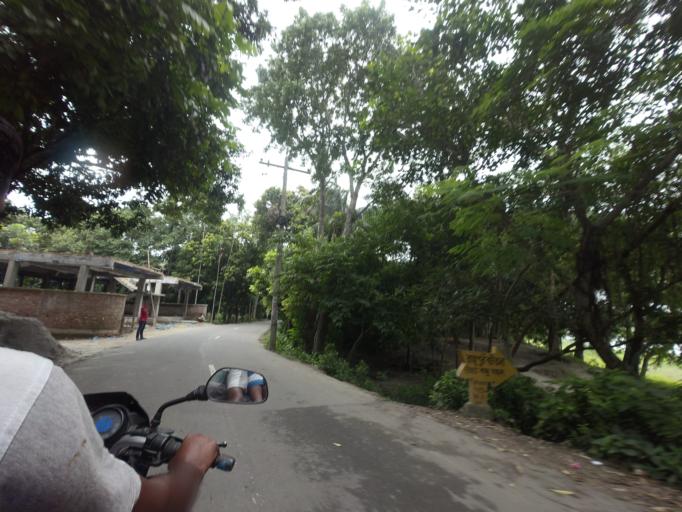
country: BD
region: Khulna
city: Kalia
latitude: 23.1766
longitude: 89.6470
